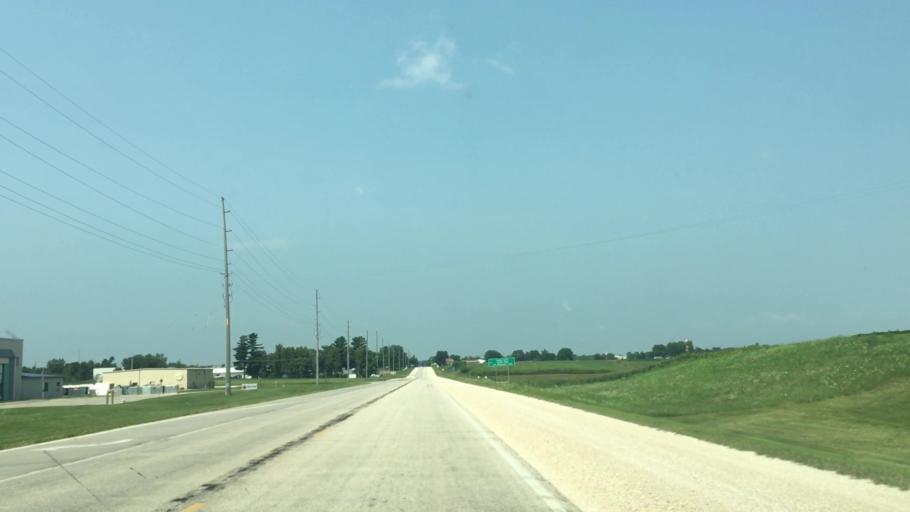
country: US
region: Iowa
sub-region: Fayette County
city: West Union
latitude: 42.9417
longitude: -91.8142
